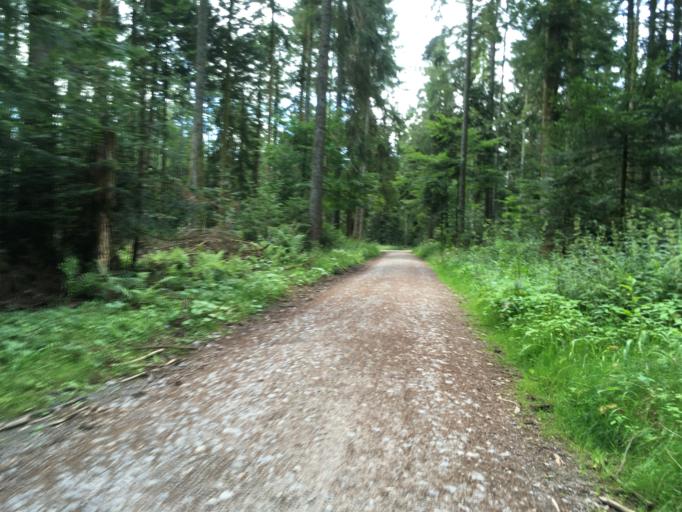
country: DE
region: Baden-Wuerttemberg
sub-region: Karlsruhe Region
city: Freudenstadt
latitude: 48.4364
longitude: 8.4070
